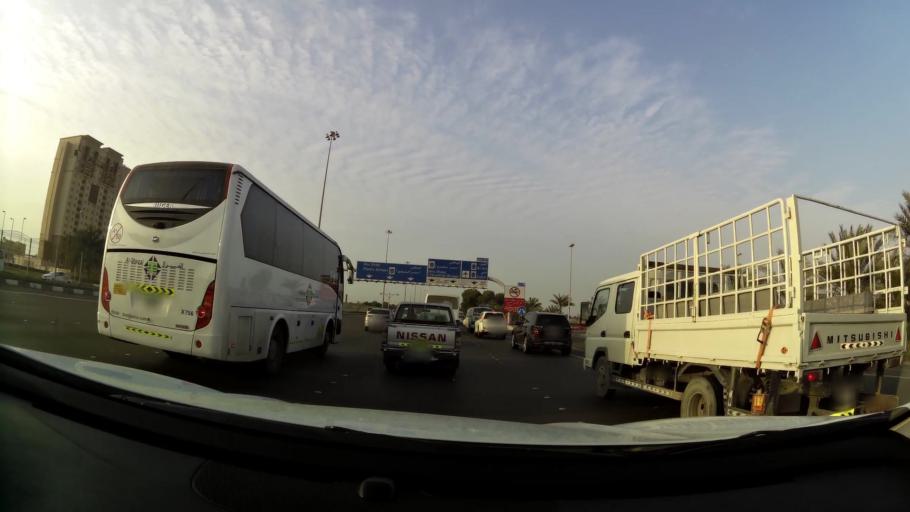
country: AE
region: Abu Dhabi
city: Abu Dhabi
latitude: 24.3823
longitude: 54.5247
